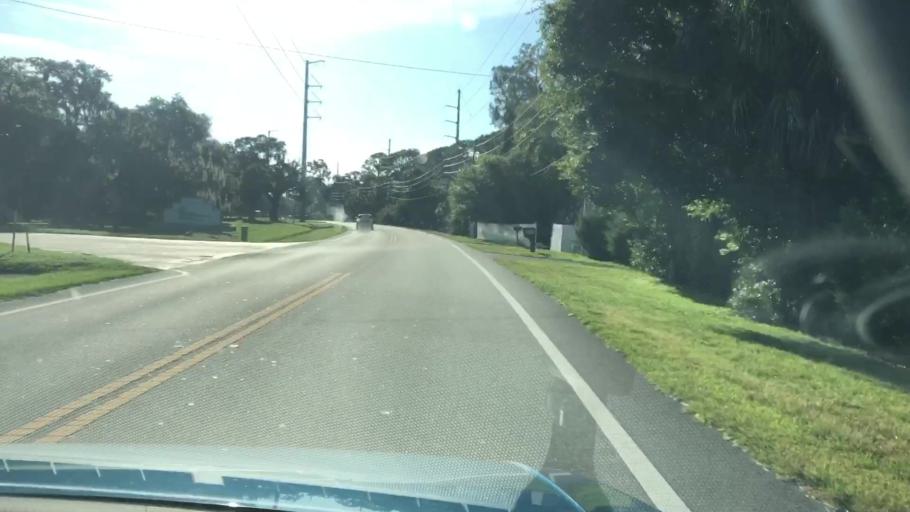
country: US
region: Florida
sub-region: Lake County
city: Eustis
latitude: 28.8742
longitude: -81.7042
